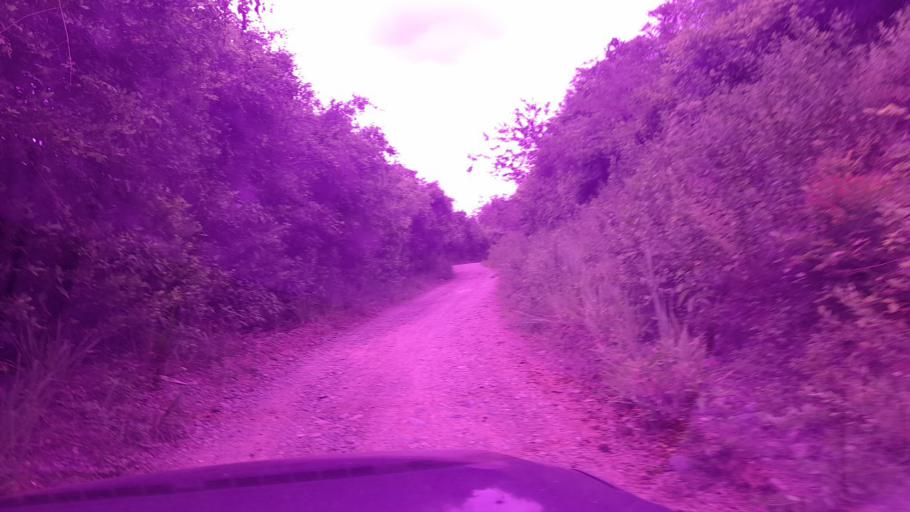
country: CO
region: Valle del Cauca
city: Andalucia
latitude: 4.1680
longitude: -76.0874
